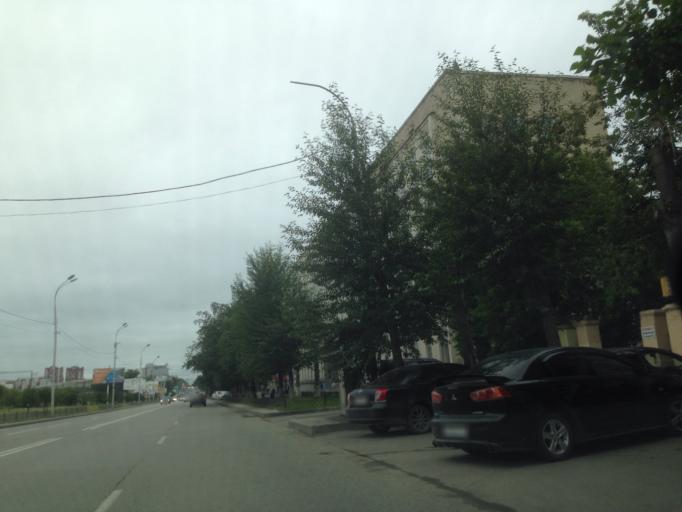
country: RU
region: Sverdlovsk
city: Yekaterinburg
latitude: 56.8412
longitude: 60.6322
